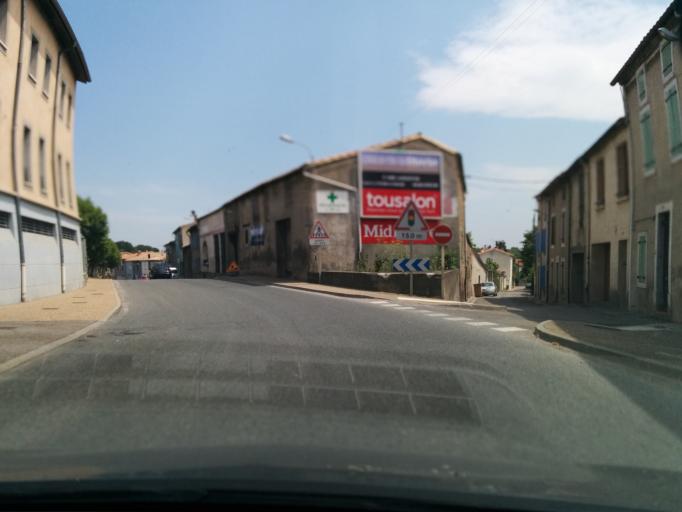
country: FR
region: Languedoc-Roussillon
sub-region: Departement de l'Aude
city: Alzonne
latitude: 43.2538
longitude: 2.1758
